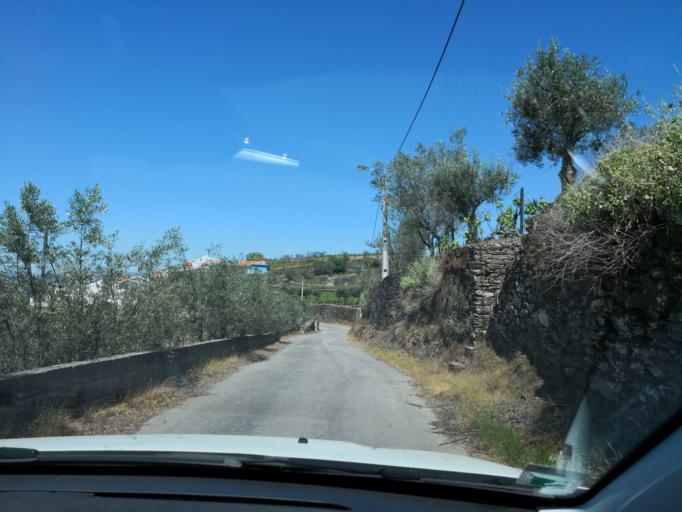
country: PT
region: Vila Real
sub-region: Santa Marta de Penaguiao
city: Santa Marta de Penaguiao
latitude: 41.2205
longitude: -7.7378
